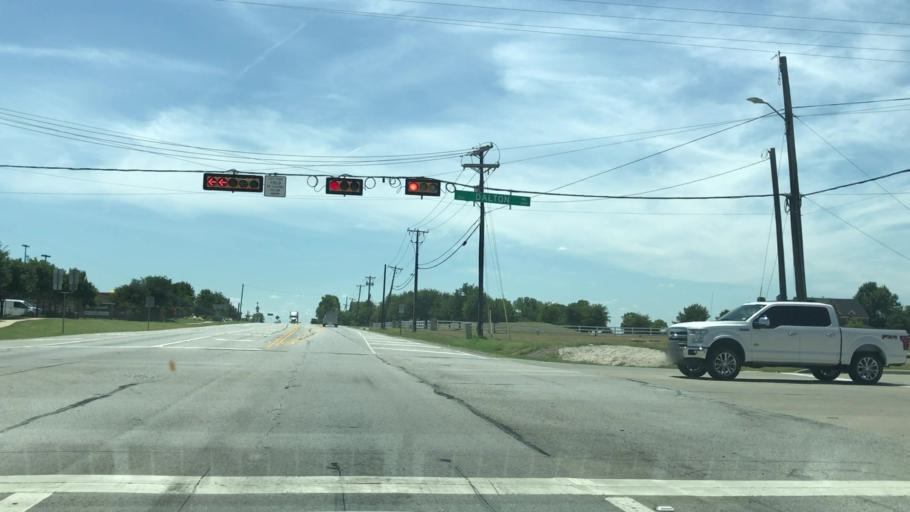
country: US
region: Texas
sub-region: Rockwall County
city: Rockwall
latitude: 32.9658
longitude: -96.4648
